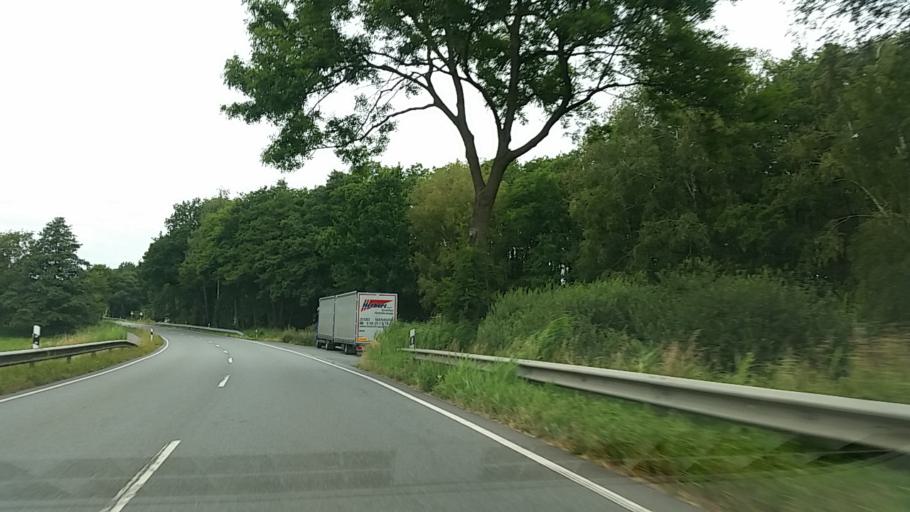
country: DE
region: Lower Saxony
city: Beverstedt
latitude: 53.4265
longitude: 8.8867
